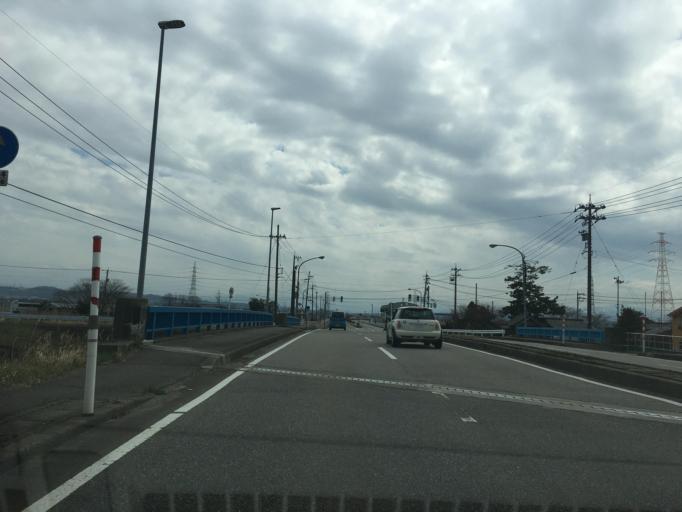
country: JP
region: Toyama
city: Kuragaki-kosugi
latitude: 36.7436
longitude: 137.1297
